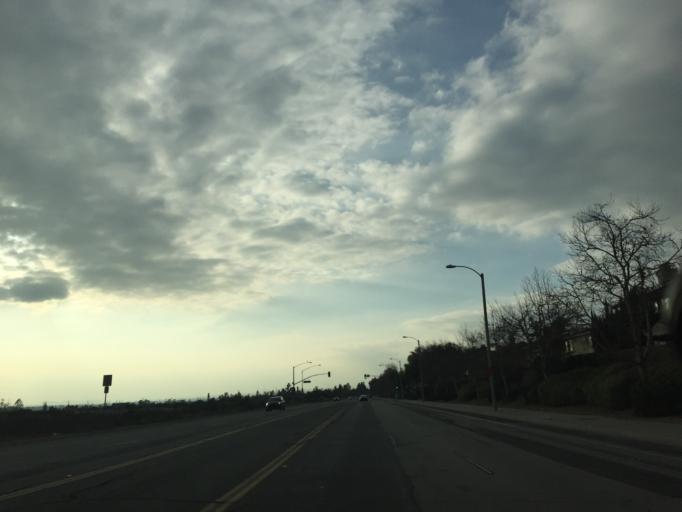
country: US
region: California
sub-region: San Bernardino County
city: Mentone
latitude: 34.1098
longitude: -117.1590
